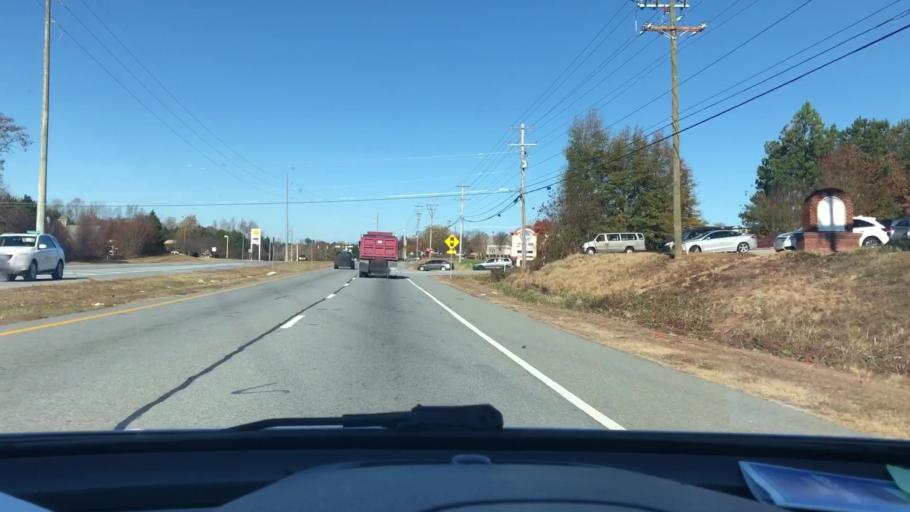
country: US
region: Georgia
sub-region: Forsyth County
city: Cumming
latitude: 34.1216
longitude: -84.1718
